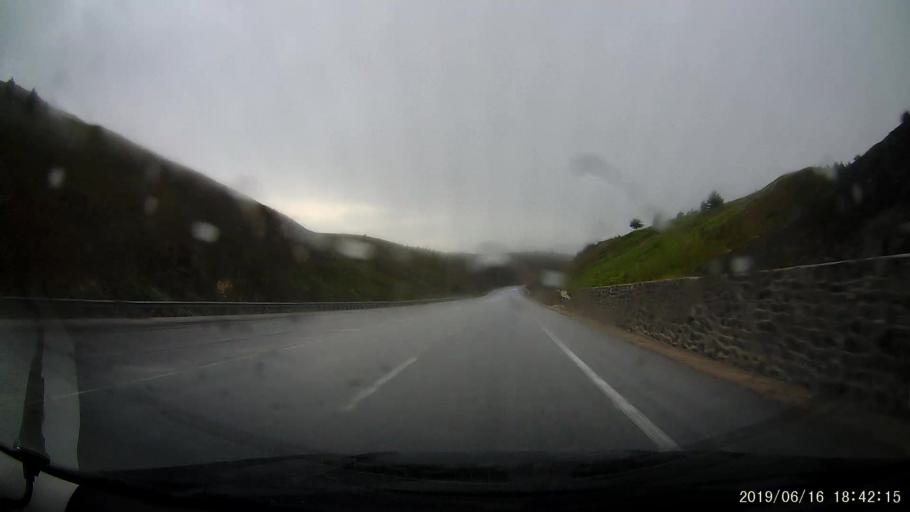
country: TR
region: Erzincan
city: Doganbeyli
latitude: 39.8699
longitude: 39.1138
